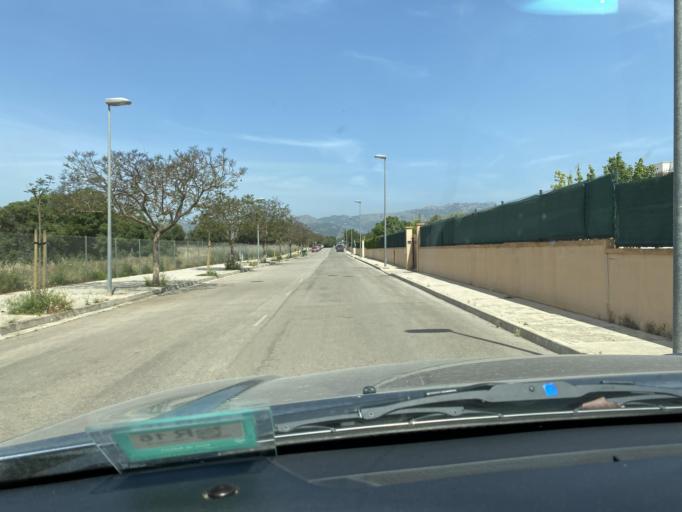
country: ES
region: Balearic Islands
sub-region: Illes Balears
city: Marratxi
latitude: 39.6347
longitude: 2.7039
